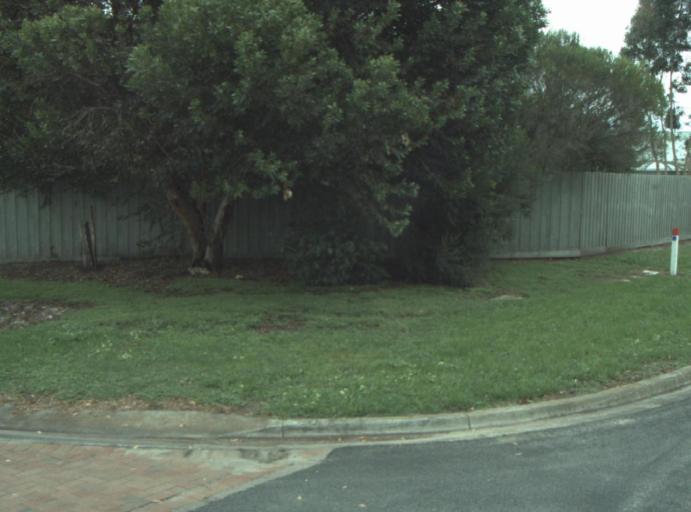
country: AU
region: Victoria
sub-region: Greater Geelong
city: Breakwater
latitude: -38.1944
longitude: 144.3870
